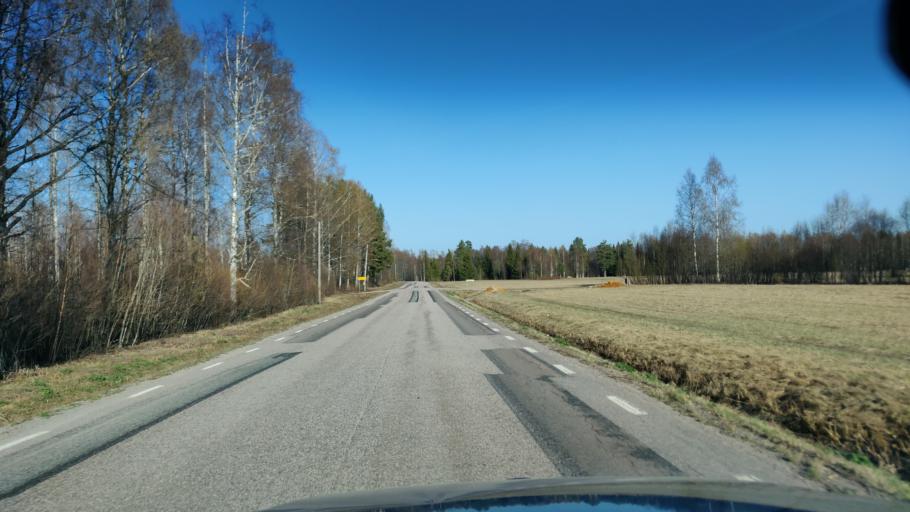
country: SE
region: Vaermland
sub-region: Munkfors Kommun
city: Munkfors
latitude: 59.9668
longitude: 13.4724
